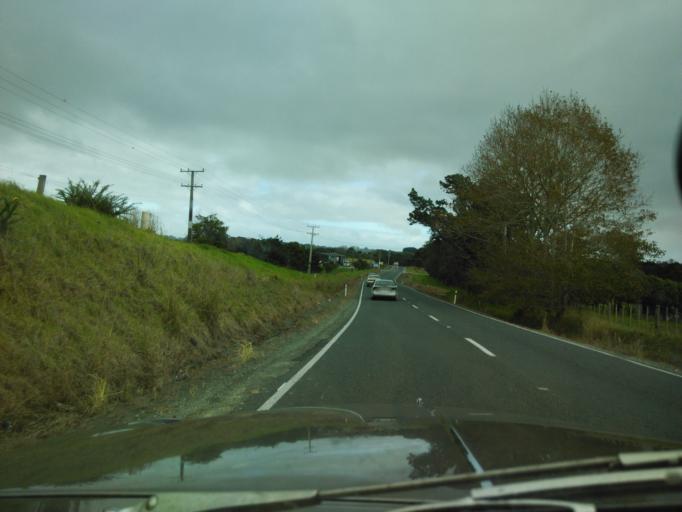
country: NZ
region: Auckland
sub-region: Auckland
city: Wellsford
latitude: -36.1367
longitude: 174.5177
